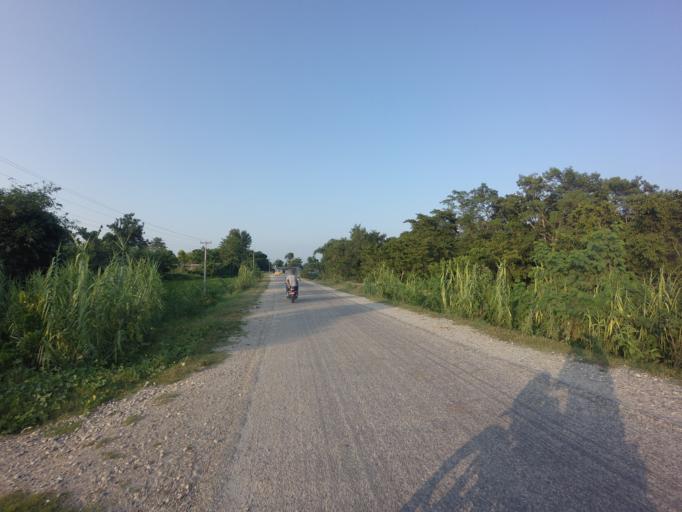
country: NP
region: Far Western
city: Tikapur
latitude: 28.4539
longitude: 81.0731
